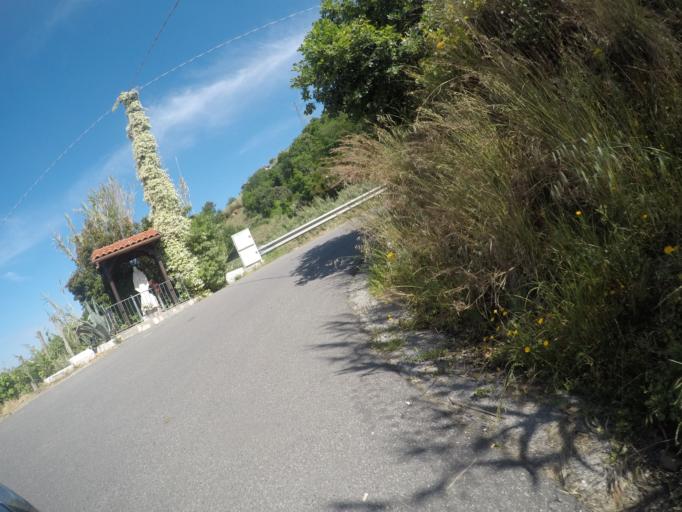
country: IT
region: Tuscany
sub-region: Provincia di Massa-Carrara
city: Massa
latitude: 44.0490
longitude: 10.1196
